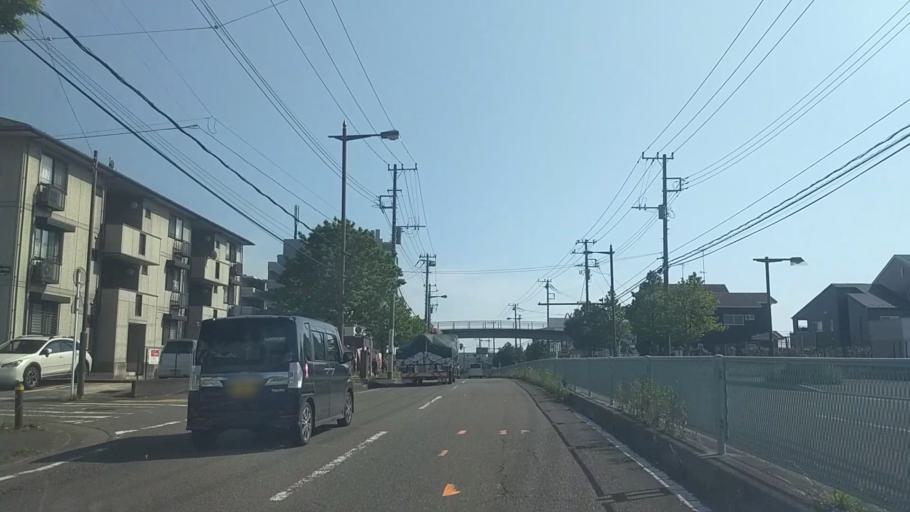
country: JP
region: Kanagawa
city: Fujisawa
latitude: 35.3530
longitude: 139.5013
